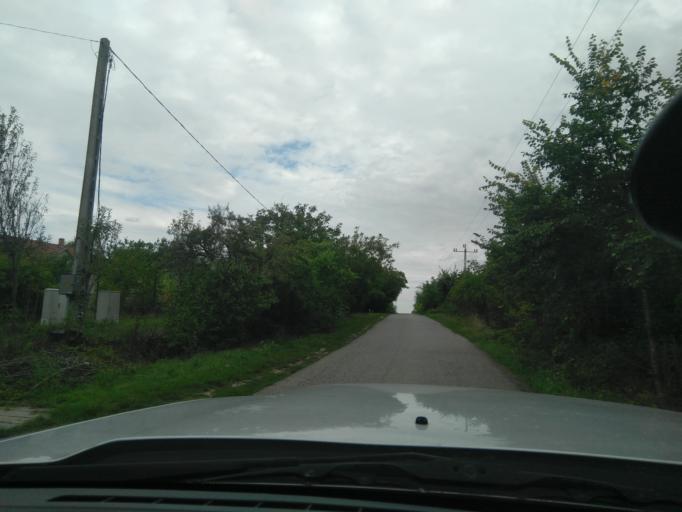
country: HU
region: Fejer
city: Martonvasar
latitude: 47.3502
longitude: 18.7700
